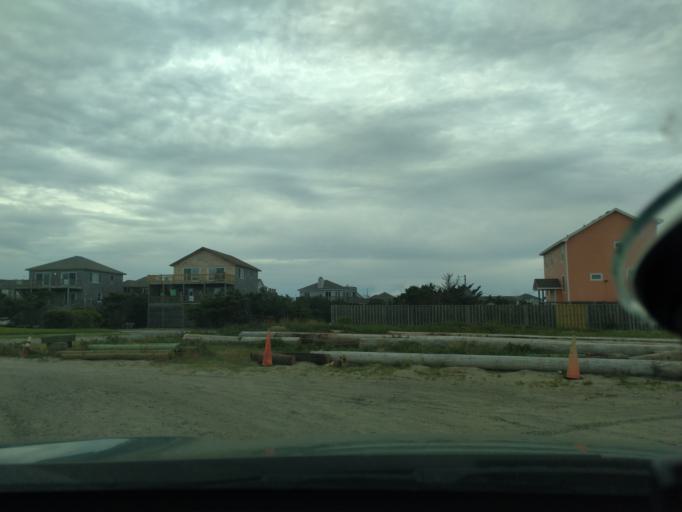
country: US
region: North Carolina
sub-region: Dare County
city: Buxton
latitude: 35.3476
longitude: -75.5019
